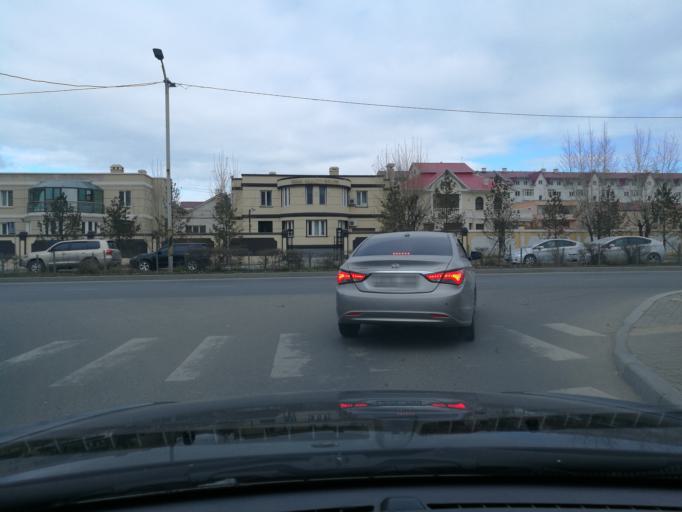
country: MN
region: Ulaanbaatar
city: Ulaanbaatar
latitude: 47.9041
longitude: 106.9206
